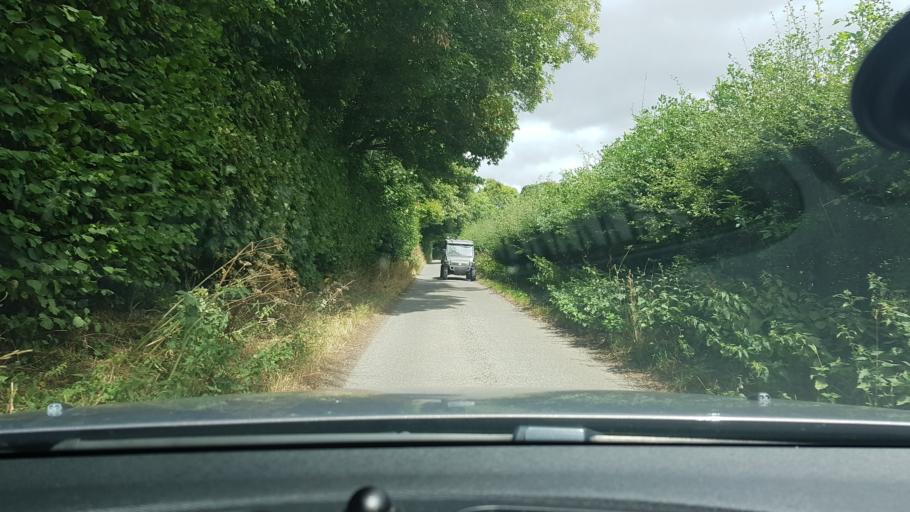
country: GB
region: England
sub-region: West Berkshire
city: Hungerford
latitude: 51.4373
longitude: -1.5169
